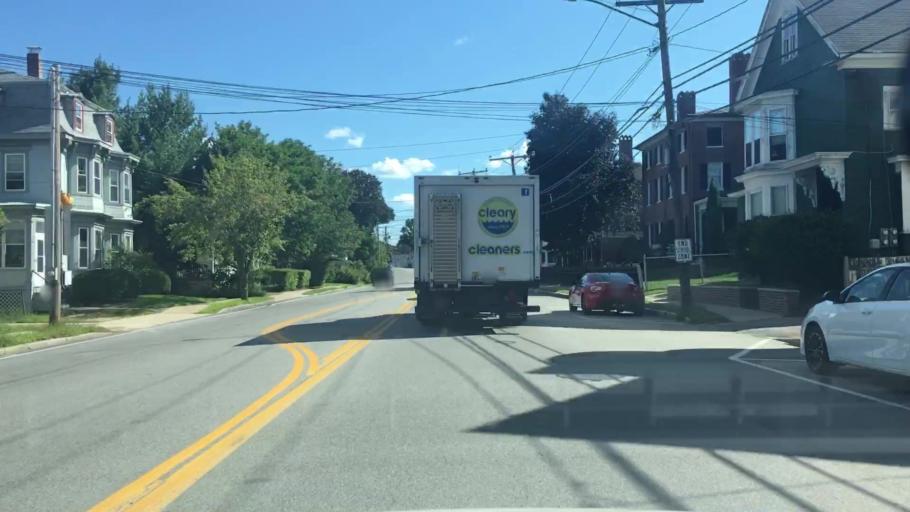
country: US
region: New Hampshire
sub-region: Strafford County
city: Dover
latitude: 43.1903
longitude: -70.8740
